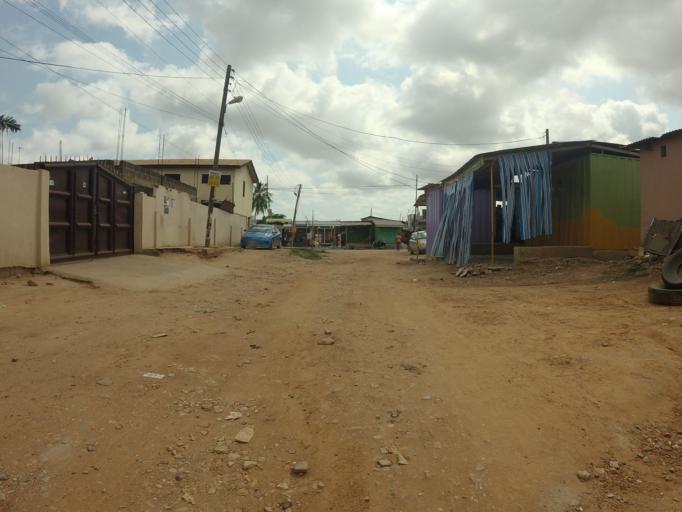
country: GH
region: Greater Accra
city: Dome
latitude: 5.6148
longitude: -0.2458
